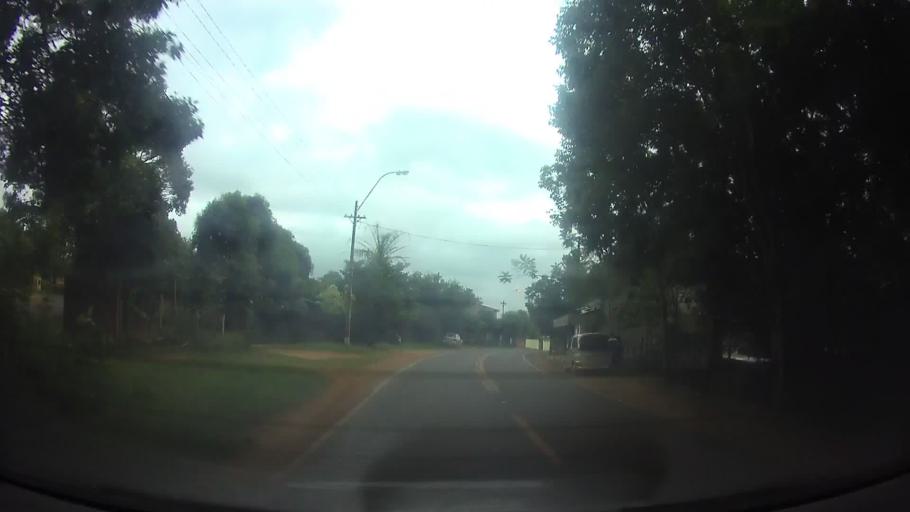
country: PY
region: Paraguari
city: Acahay
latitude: -25.9154
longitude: -57.1146
